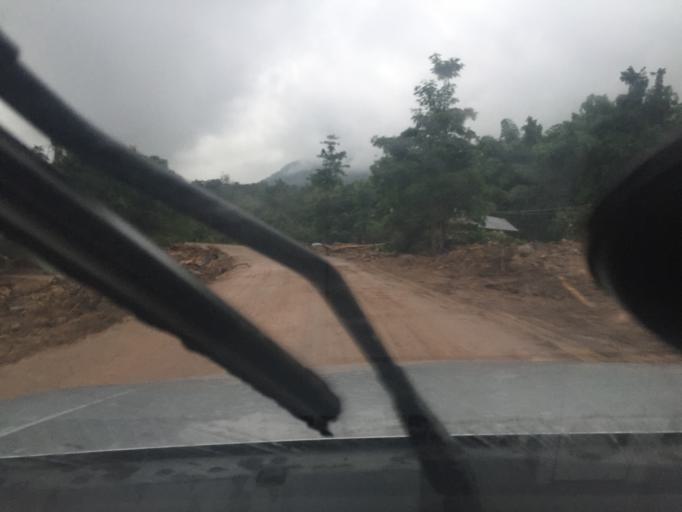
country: LA
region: Attapu
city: Attapu
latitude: 15.0909
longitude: 106.8261
